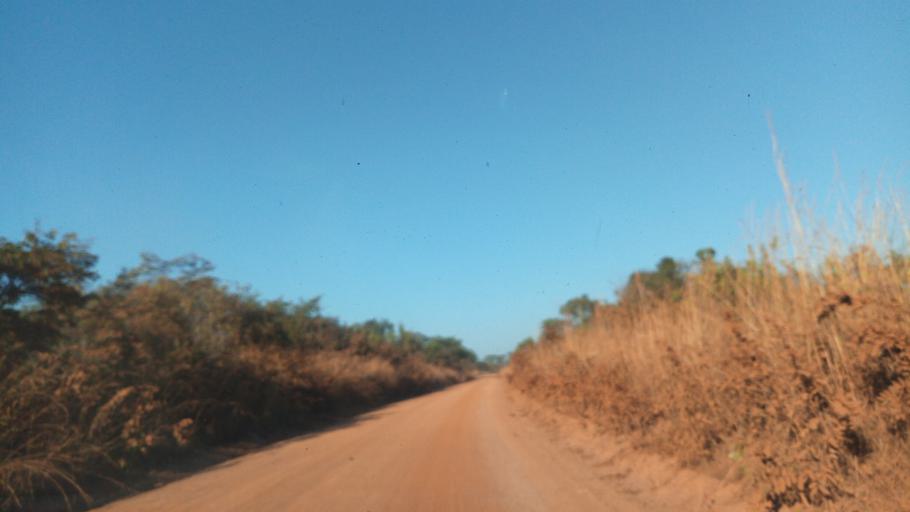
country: ZM
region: Luapula
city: Mwense
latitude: -10.4964
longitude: 28.4840
